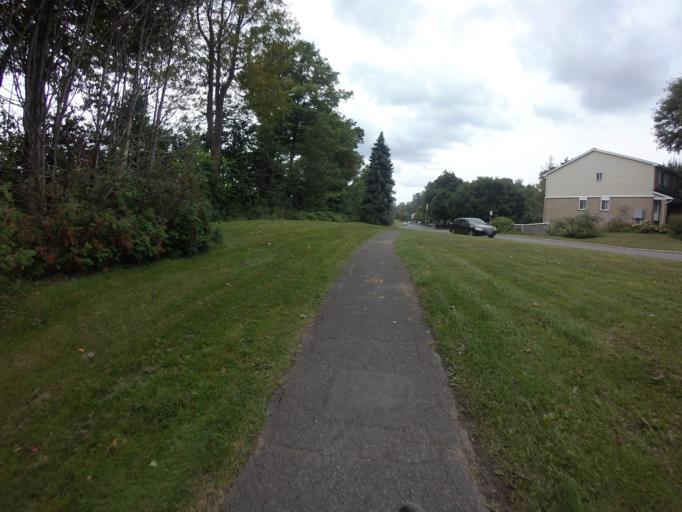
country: CA
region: Quebec
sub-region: Outaouais
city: Gatineau
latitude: 45.4787
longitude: -75.5228
